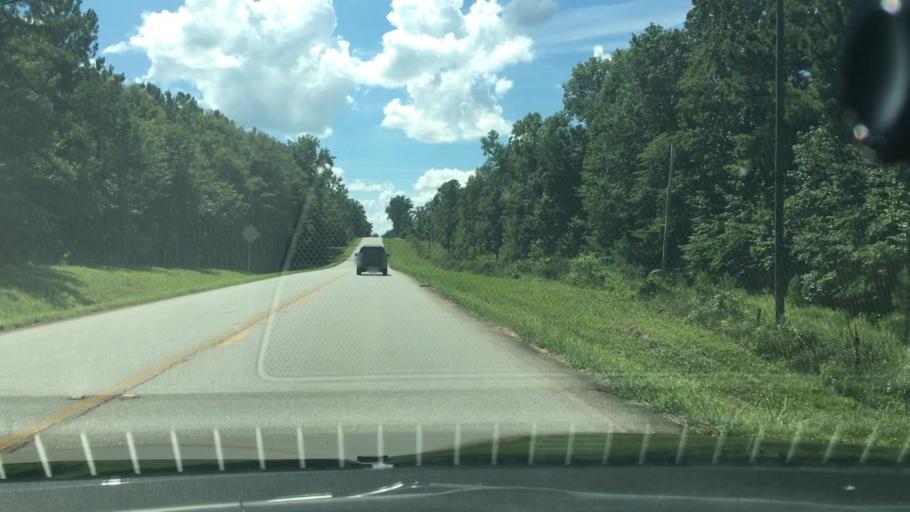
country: US
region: Georgia
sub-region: Jasper County
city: Monticello
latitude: 33.3053
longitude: -83.5968
